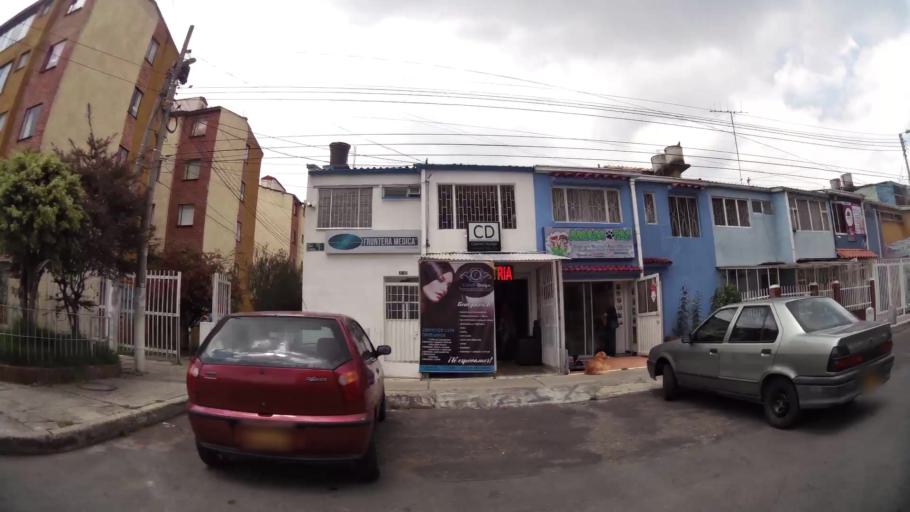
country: CO
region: Cundinamarca
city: La Calera
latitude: 4.7325
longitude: -74.0312
